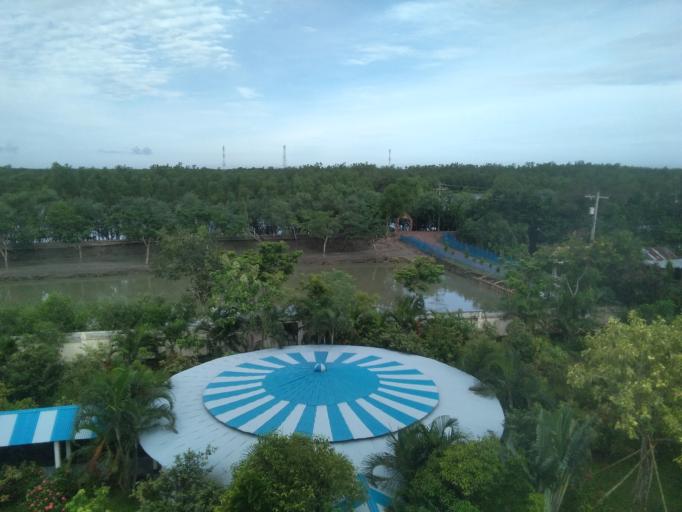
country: IN
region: West Bengal
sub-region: North 24 Parganas
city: Gosaba
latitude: 22.2687
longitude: 89.2044
